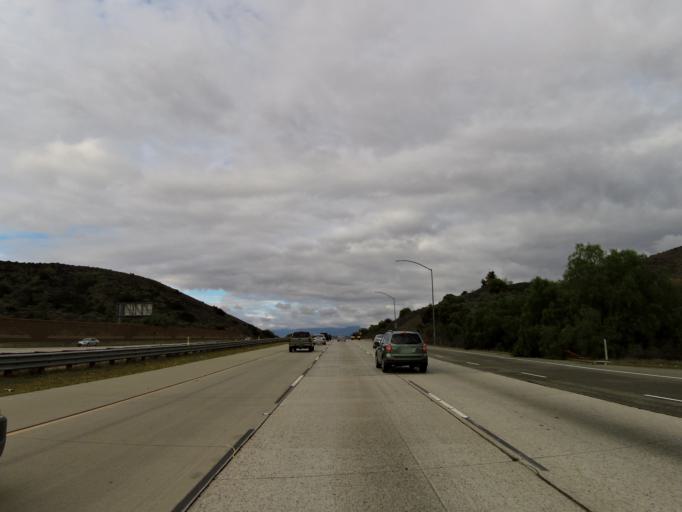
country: US
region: California
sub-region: Ventura County
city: Moorpark
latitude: 34.2694
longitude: -118.8531
